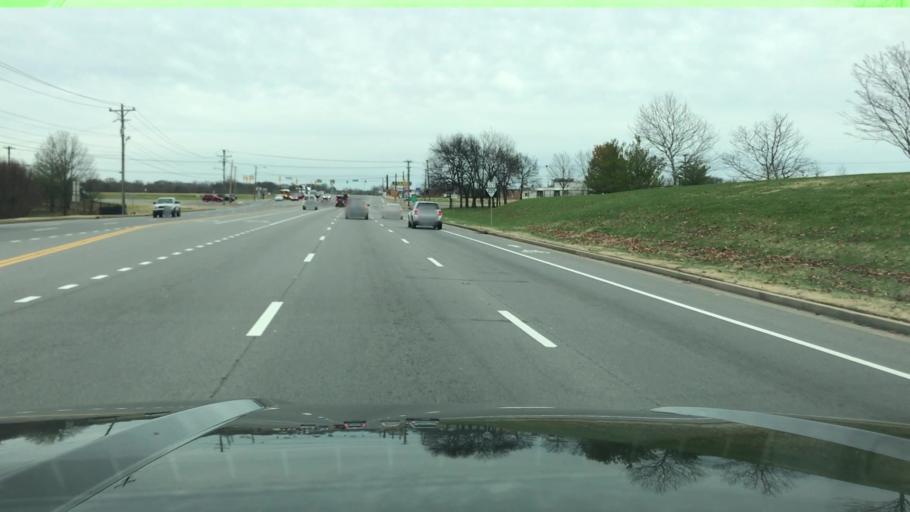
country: US
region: Tennessee
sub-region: Davidson County
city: Oak Hill
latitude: 36.1071
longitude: -86.6753
